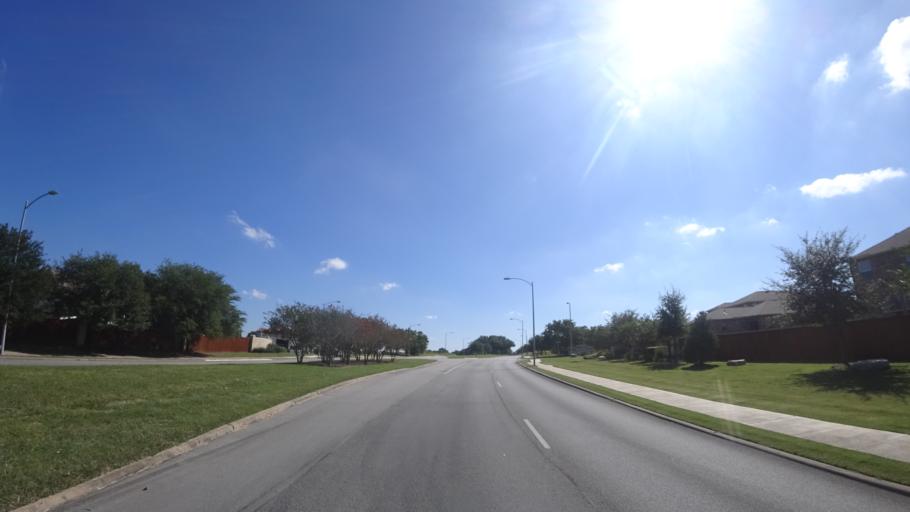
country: US
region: Texas
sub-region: Travis County
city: Manor
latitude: 30.3482
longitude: -97.6140
